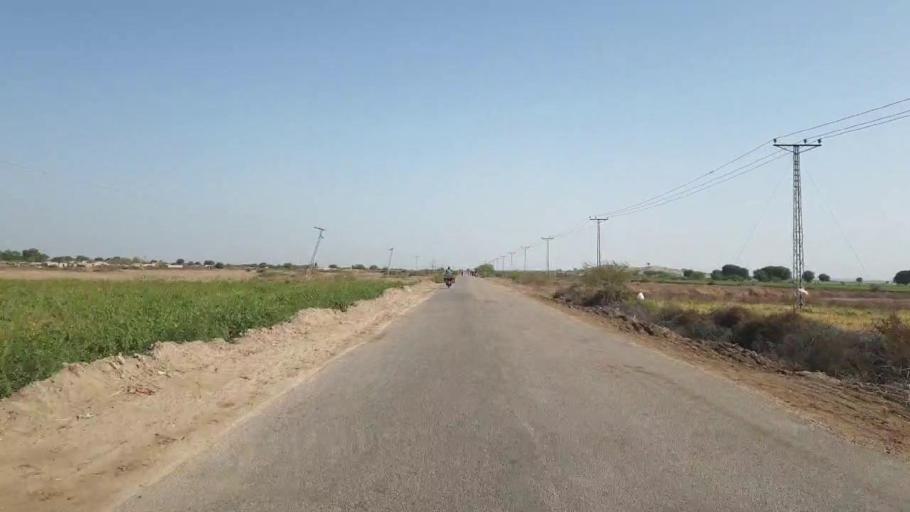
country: PK
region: Sindh
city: Umarkot
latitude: 25.4186
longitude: 69.7341
